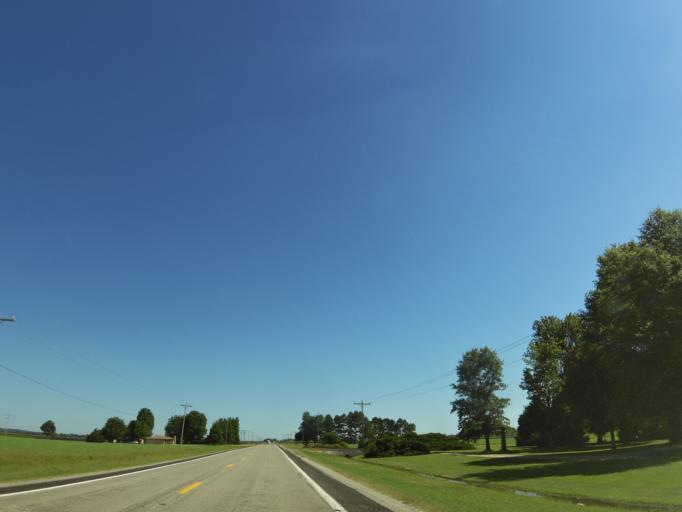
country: US
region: Arkansas
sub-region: Clay County
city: Piggott
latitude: 36.3933
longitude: -90.1483
